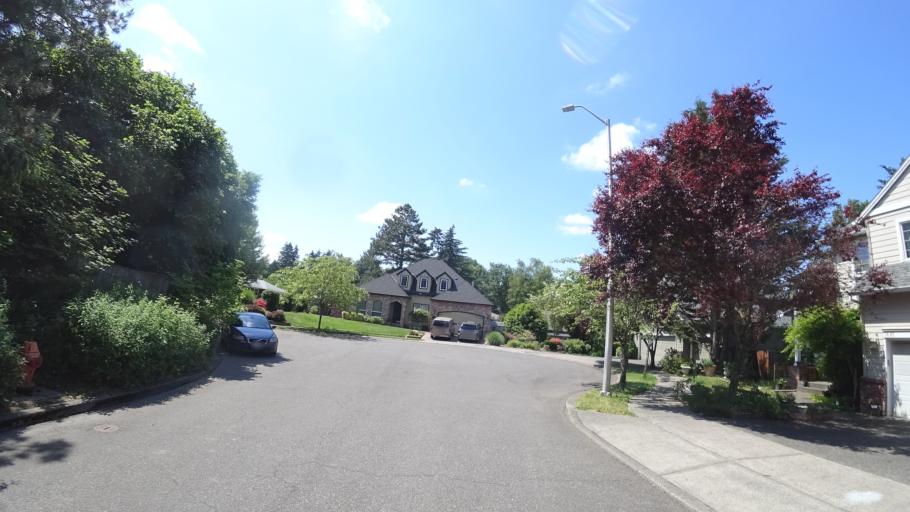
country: US
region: Oregon
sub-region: Clackamas County
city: Lake Oswego
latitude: 45.4377
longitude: -122.6972
